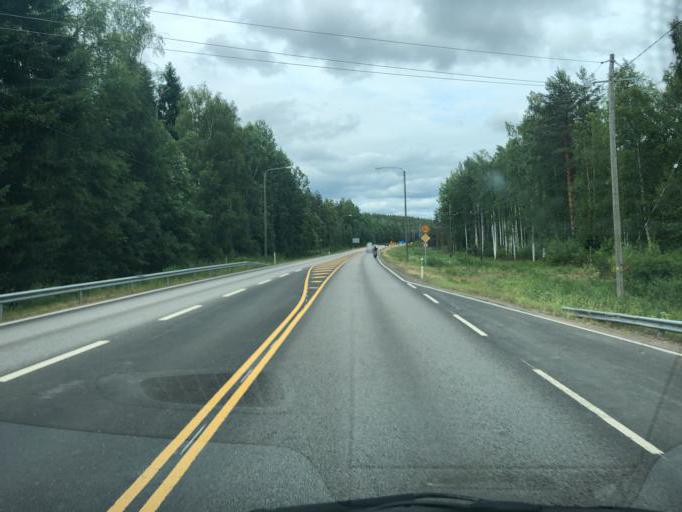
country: FI
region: Kymenlaakso
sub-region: Kouvola
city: Kouvola
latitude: 60.9300
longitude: 26.8013
